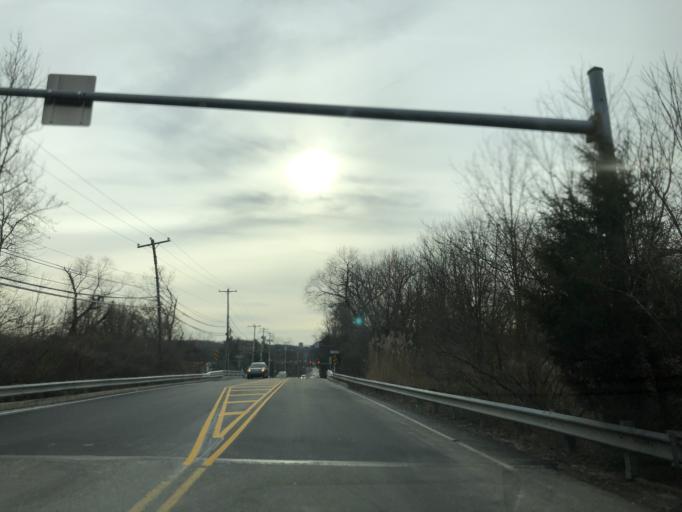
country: US
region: Pennsylvania
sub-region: Chester County
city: Exton
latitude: 40.0232
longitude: -75.6441
